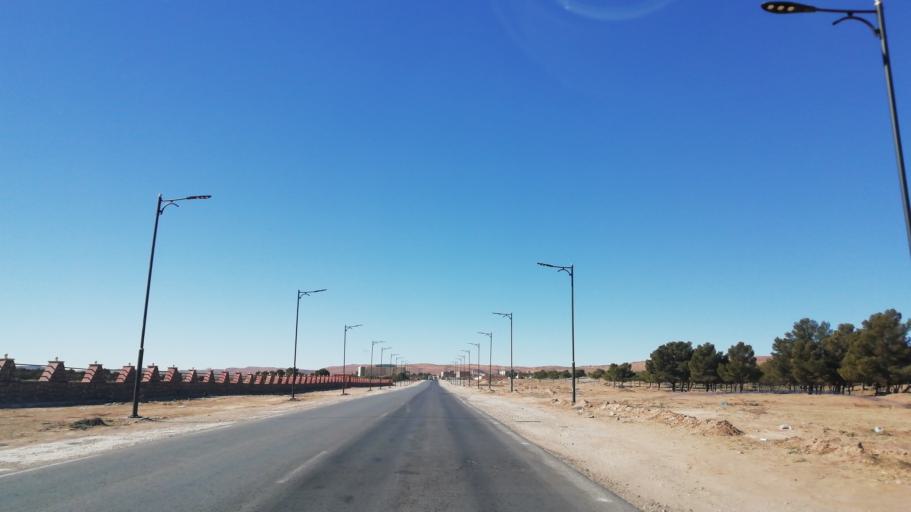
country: DZ
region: El Bayadh
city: El Bayadh
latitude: 33.7294
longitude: 1.5473
